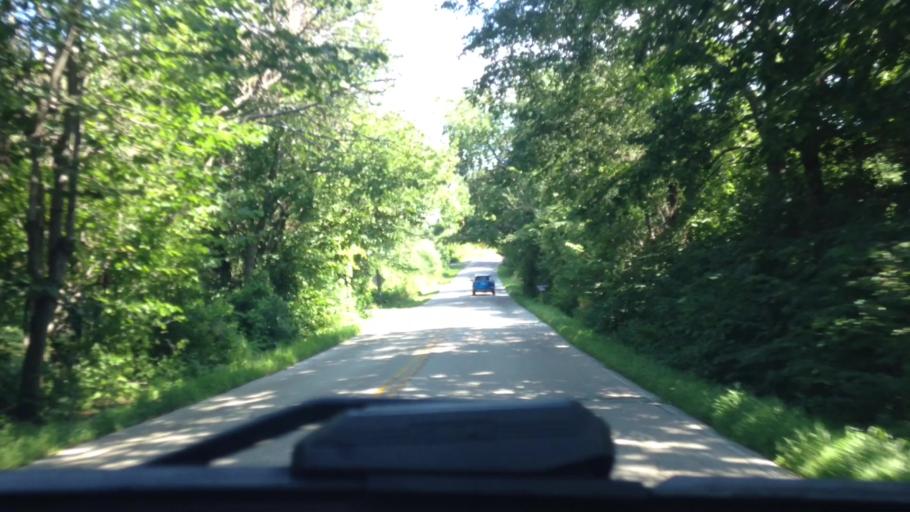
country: US
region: Wisconsin
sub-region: Washington County
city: West Bend
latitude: 43.4105
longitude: -88.2311
